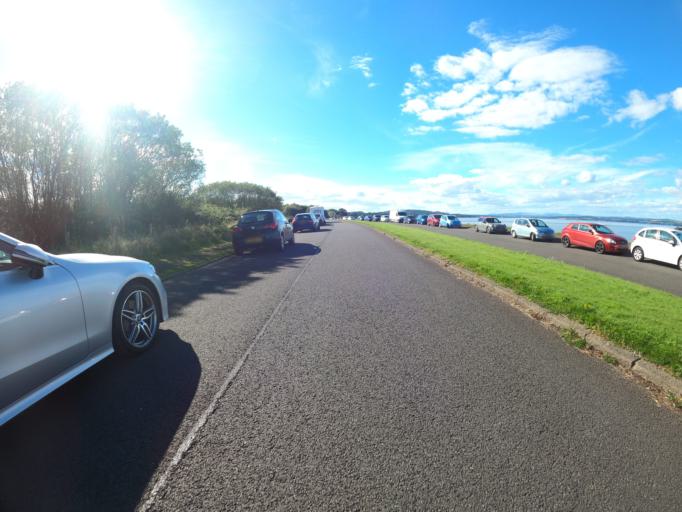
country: GB
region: Scotland
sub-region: Fife
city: Aberdour
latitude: 55.9790
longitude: -3.2816
